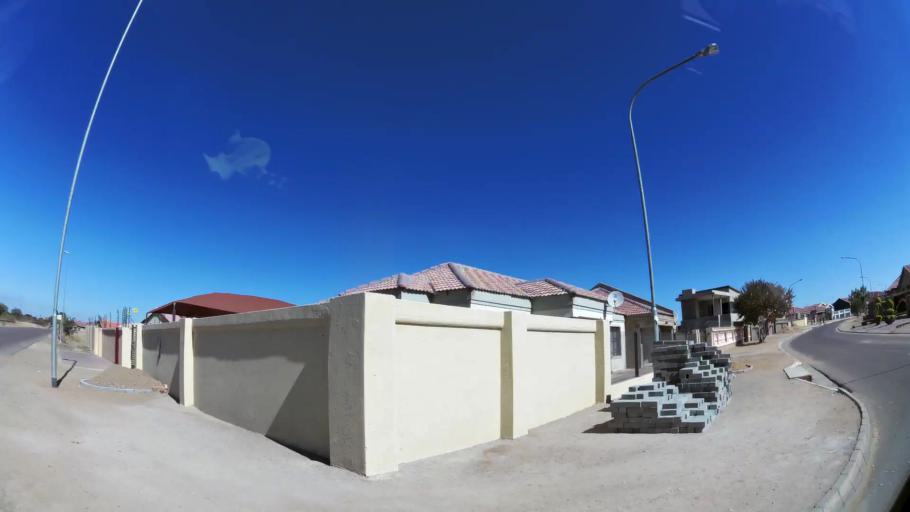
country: ZA
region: Limpopo
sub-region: Capricorn District Municipality
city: Polokwane
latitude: -23.8606
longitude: 29.4268
